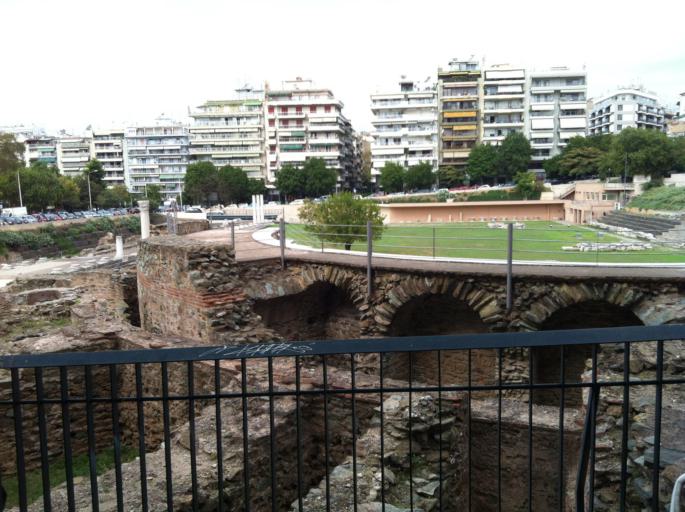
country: GR
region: Central Macedonia
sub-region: Nomos Thessalonikis
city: Sykies
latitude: 40.6374
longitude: 22.9466
